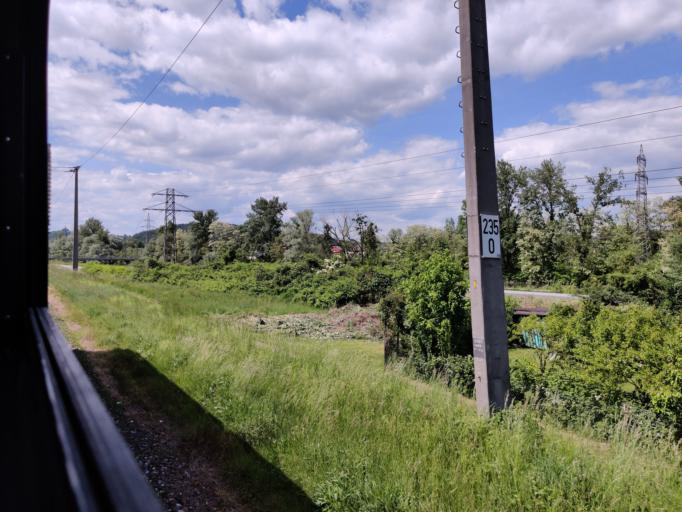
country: AT
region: Styria
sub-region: Politischer Bezirk Leibnitz
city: Wildon
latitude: 46.8837
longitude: 15.5218
